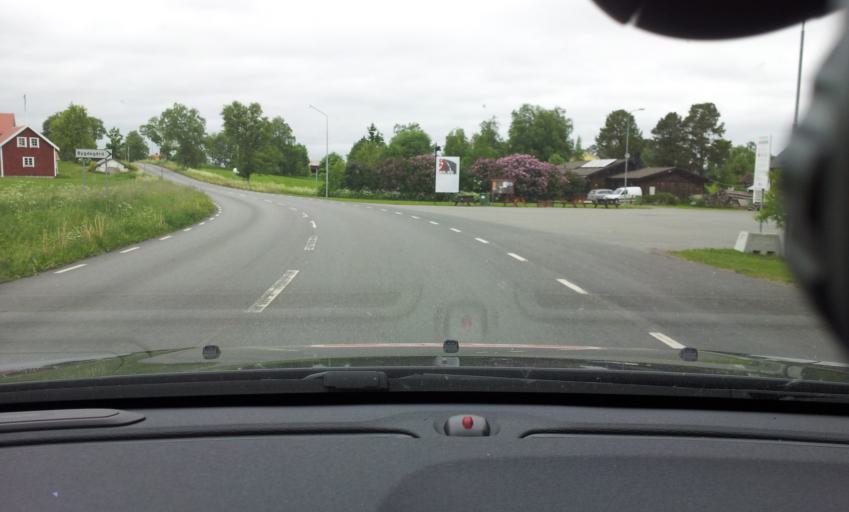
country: SE
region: Jaemtland
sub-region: Bergs Kommun
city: Hoverberg
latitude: 63.0657
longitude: 14.3283
